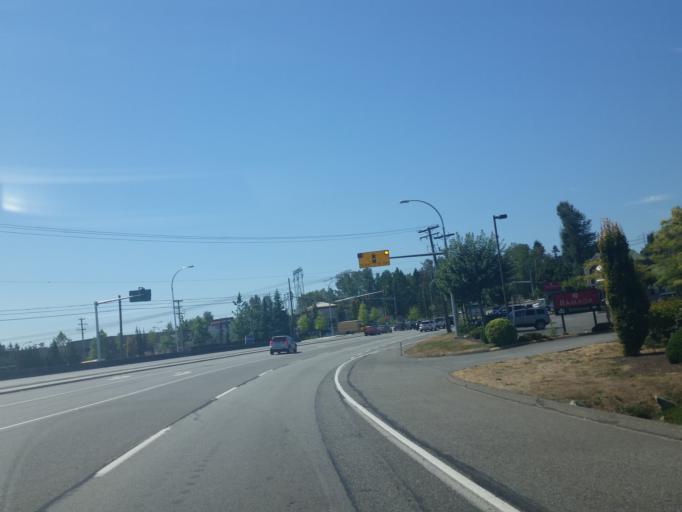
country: CA
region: British Columbia
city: Langley
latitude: 49.1050
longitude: -122.6891
